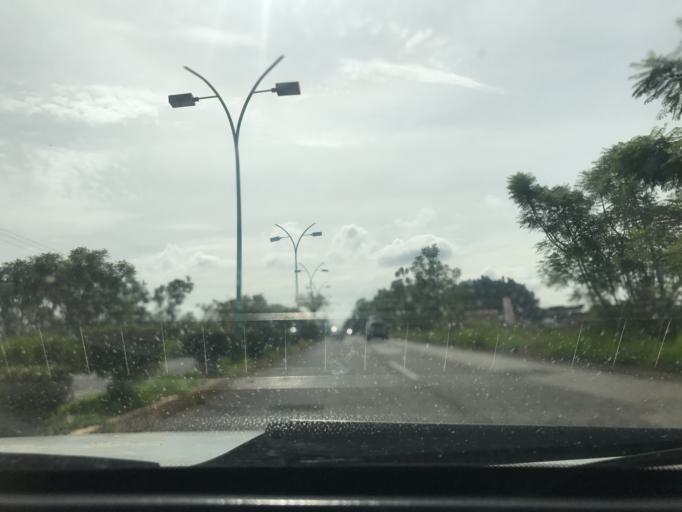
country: MX
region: Morelos
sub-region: Atlatlahucan
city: Colonia San Francisco
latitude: 18.8946
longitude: -98.9020
